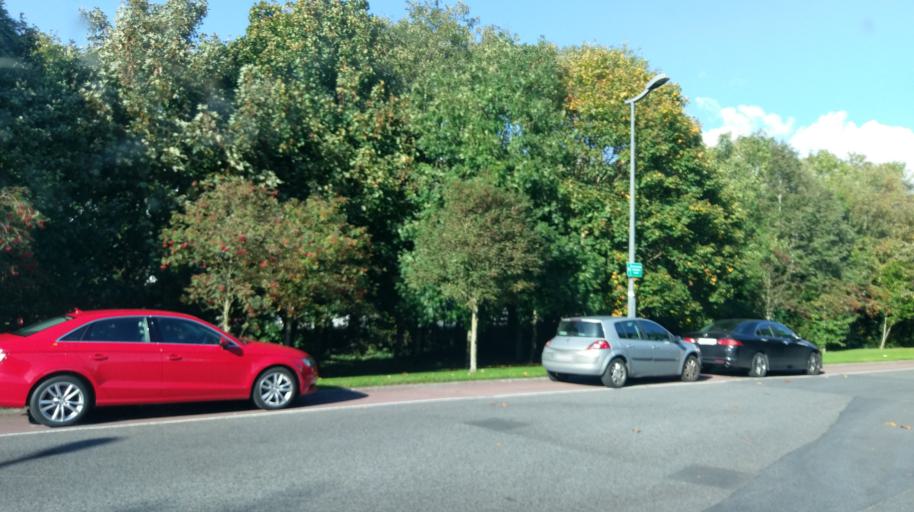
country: IE
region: Connaught
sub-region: County Galway
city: Gaillimh
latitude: 53.2864
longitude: -9.0295
